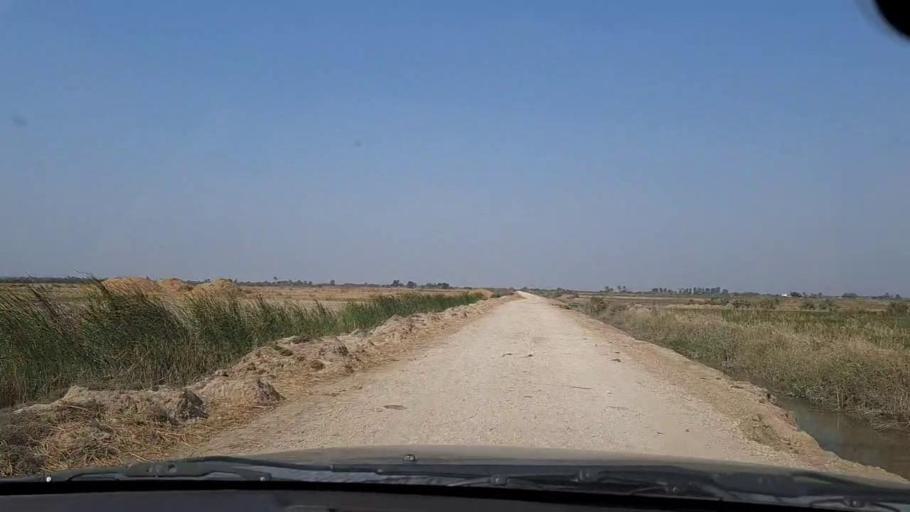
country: PK
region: Sindh
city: Mirpur Sakro
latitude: 24.3673
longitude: 67.6830
